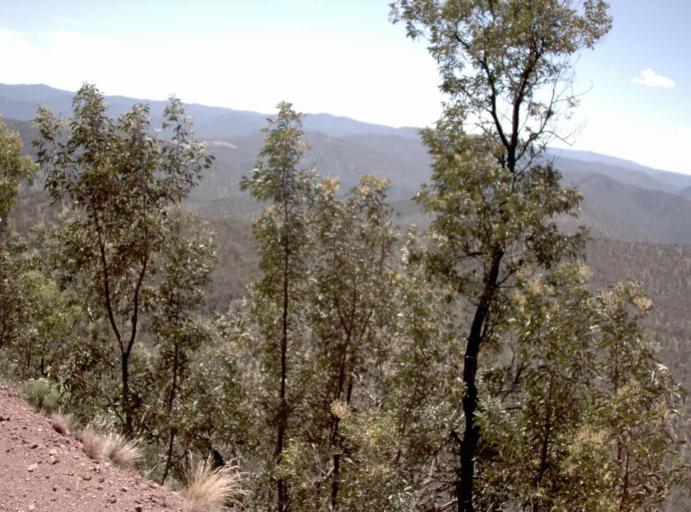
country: AU
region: New South Wales
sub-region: Snowy River
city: Jindabyne
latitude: -37.0003
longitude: 148.2992
